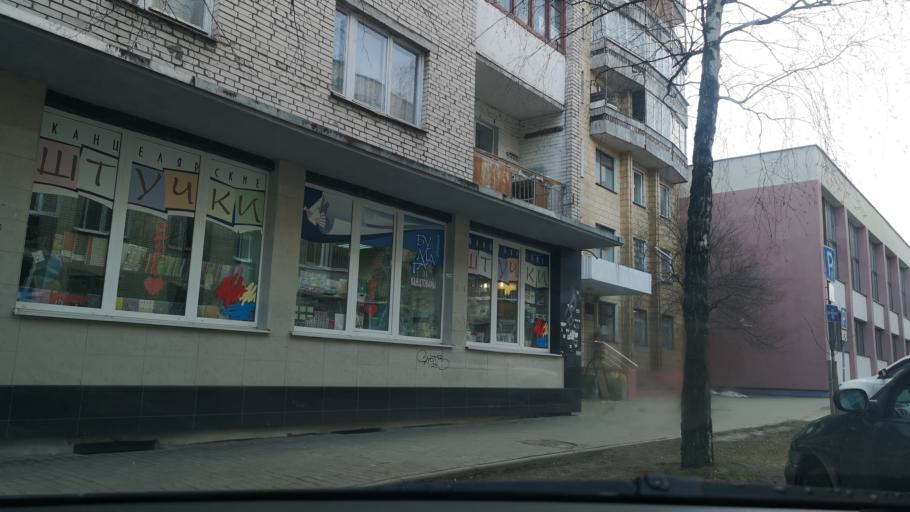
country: BY
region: Brest
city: Brest
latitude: 52.0959
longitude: 23.6952
